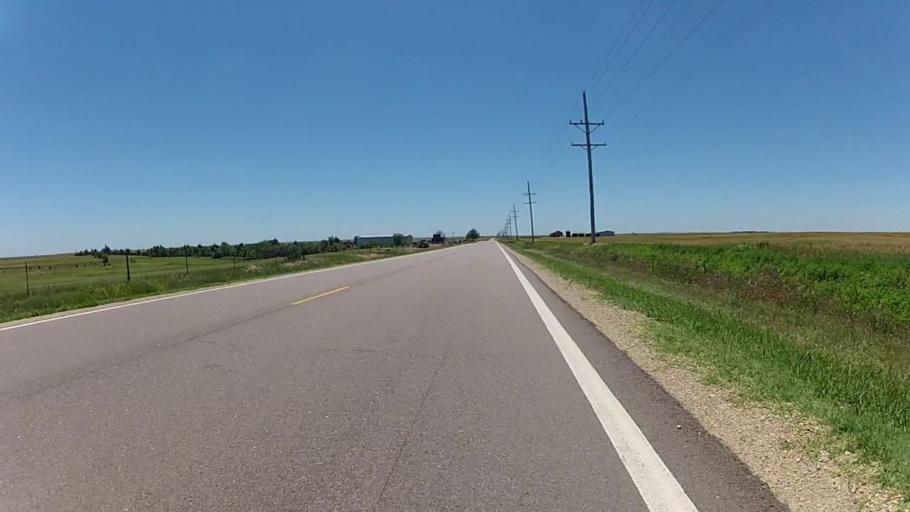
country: US
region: Kansas
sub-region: Kiowa County
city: Greensburg
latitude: 37.5083
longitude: -99.3204
